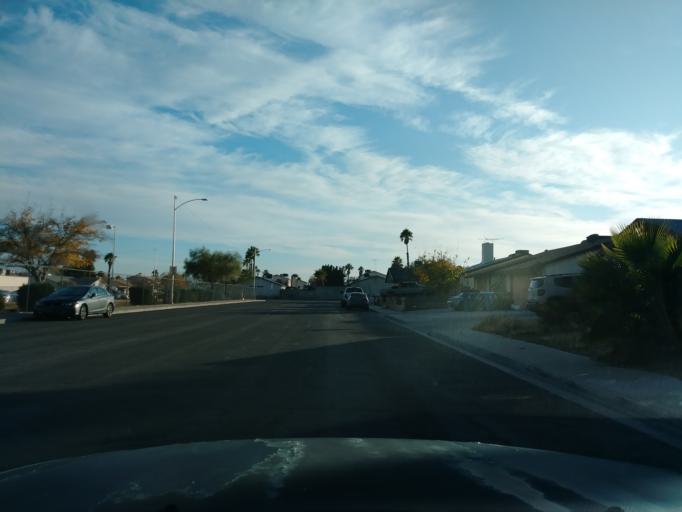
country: US
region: Nevada
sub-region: Clark County
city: Spring Valley
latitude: 36.1693
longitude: -115.2354
